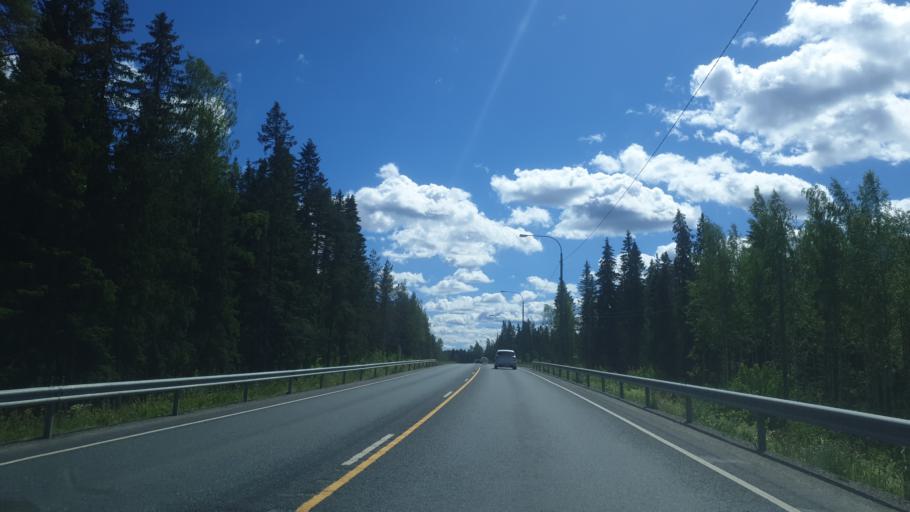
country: FI
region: Northern Savo
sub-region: Varkaus
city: Leppaevirta
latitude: 62.5445
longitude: 27.6263
